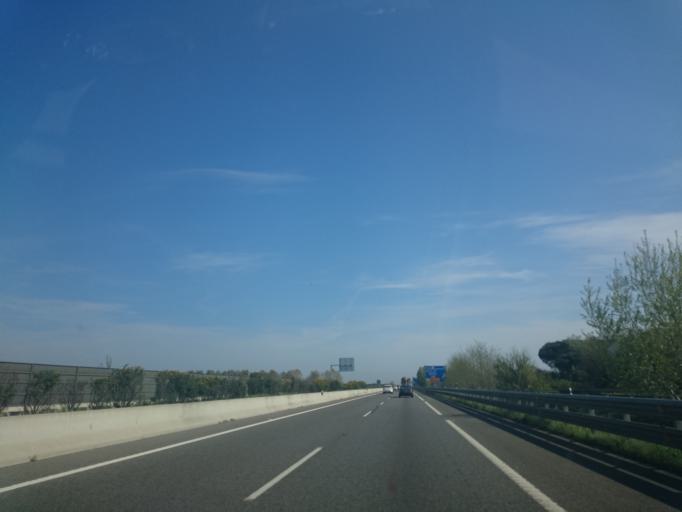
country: ES
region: Catalonia
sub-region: Provincia de Girona
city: Vilobi d'Onyar
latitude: 41.8745
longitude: 2.7792
